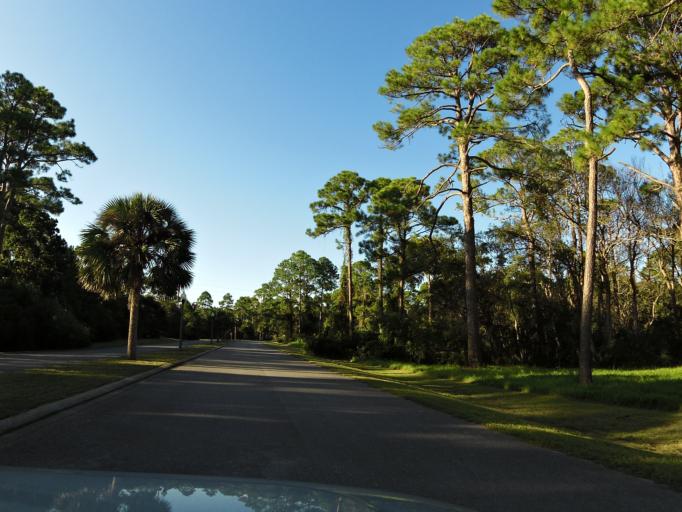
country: US
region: Florida
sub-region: Franklin County
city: Eastpoint
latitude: 29.7586
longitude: -84.8304
